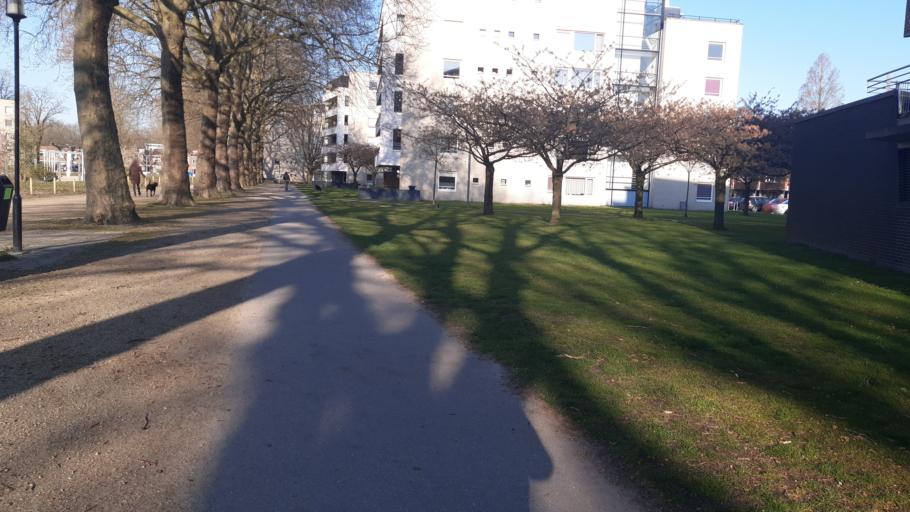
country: NL
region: North Brabant
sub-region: Gemeente Tilburg
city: Tilburg
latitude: 51.5548
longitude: 5.0672
